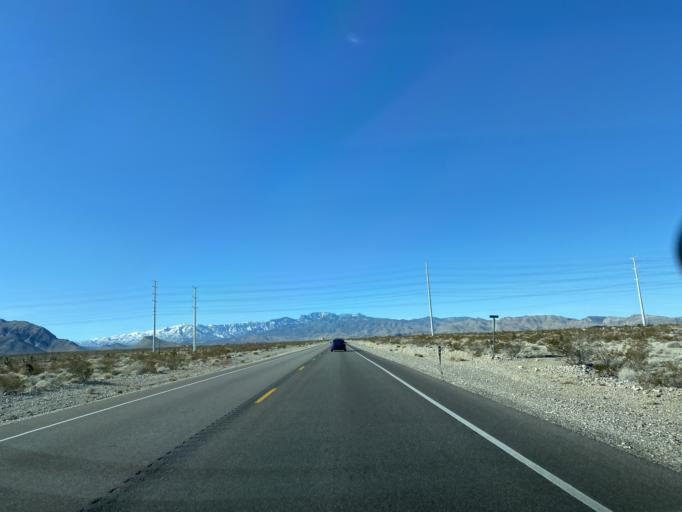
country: US
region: Nevada
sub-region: Clark County
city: Summerlin South
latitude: 36.3259
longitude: -115.3262
